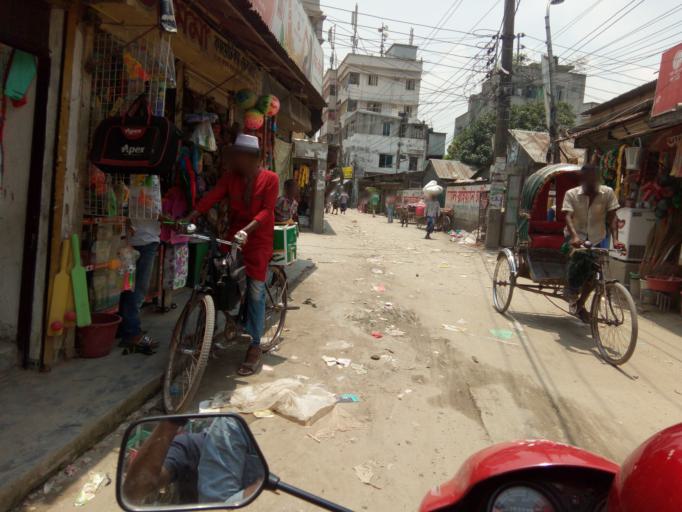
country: BD
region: Dhaka
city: Paltan
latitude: 23.7562
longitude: 90.4373
